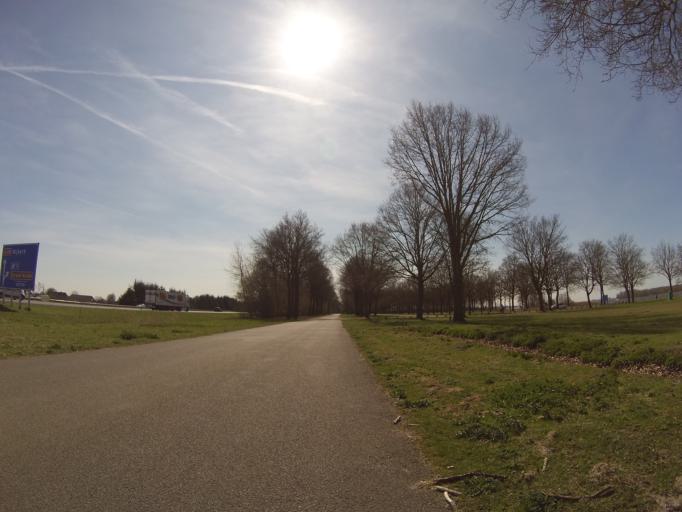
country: NL
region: Gelderland
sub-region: Gemeente Ermelo
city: Horst
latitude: 52.2772
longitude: 5.5420
